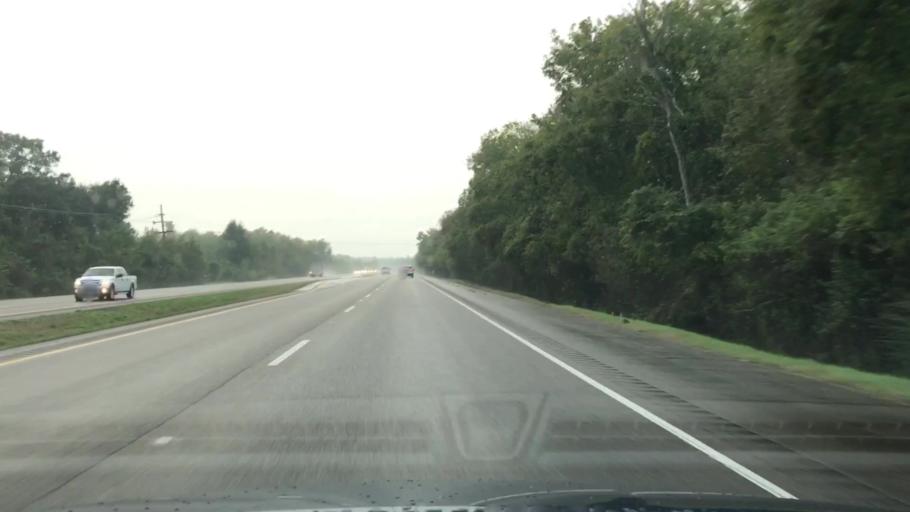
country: US
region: Louisiana
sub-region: Saint Charles Parish
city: Paradis
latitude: 29.8644
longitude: -90.4455
